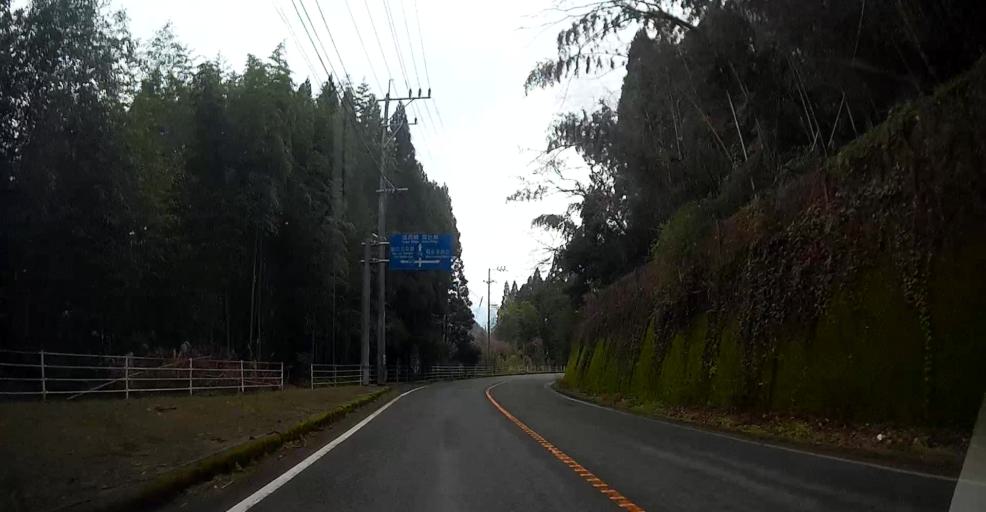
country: JP
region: Kumamoto
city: Matsubase
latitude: 32.6274
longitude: 130.8109
